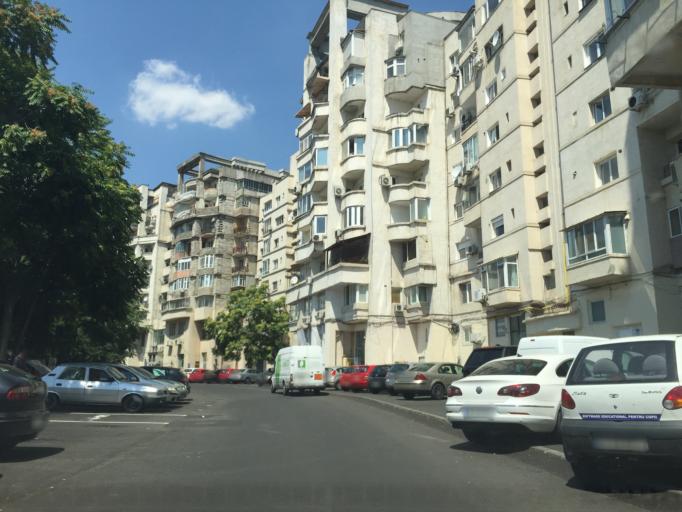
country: RO
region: Bucuresti
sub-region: Municipiul Bucuresti
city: Bucharest
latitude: 44.4249
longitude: 26.1079
